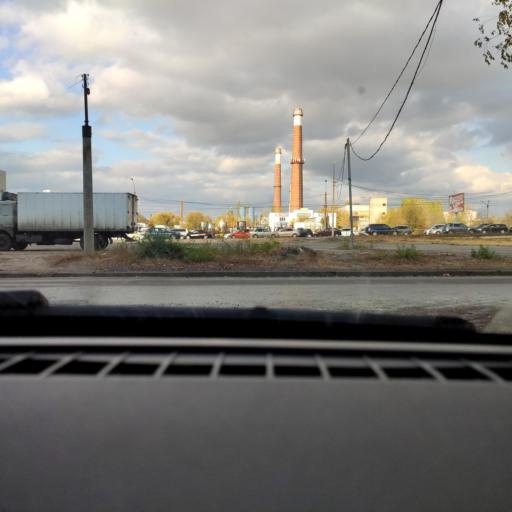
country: RU
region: Voronezj
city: Voronezh
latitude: 51.6842
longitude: 39.2684
